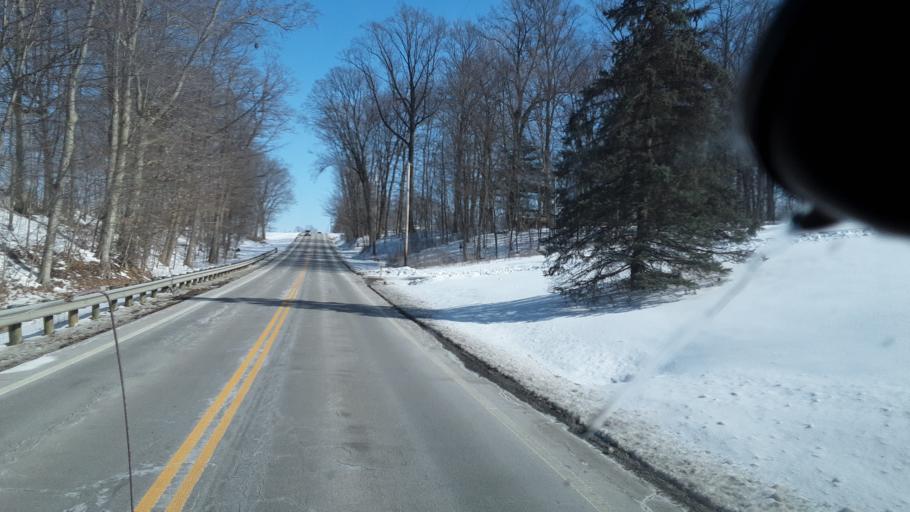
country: US
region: Ohio
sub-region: Mahoning County
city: Sebring
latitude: 40.9449
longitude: -80.9388
